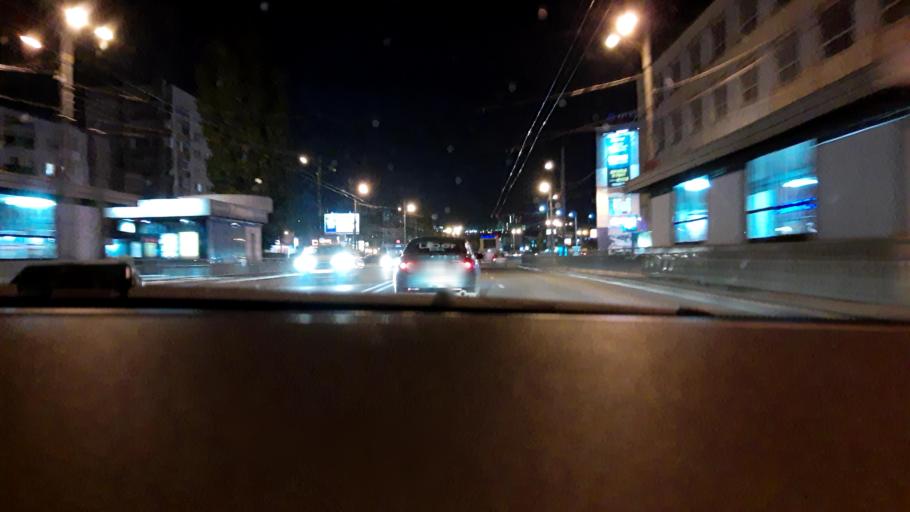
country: RU
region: Nizjnij Novgorod
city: Nizhniy Novgorod
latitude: 56.3211
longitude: 43.9248
